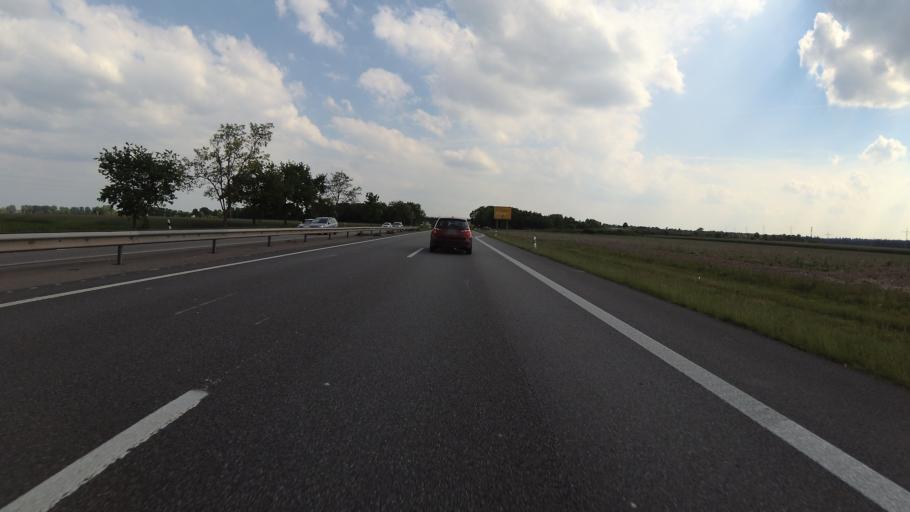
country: DE
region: Rheinland-Pfalz
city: Otterstadt
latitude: 49.3659
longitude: 8.4213
